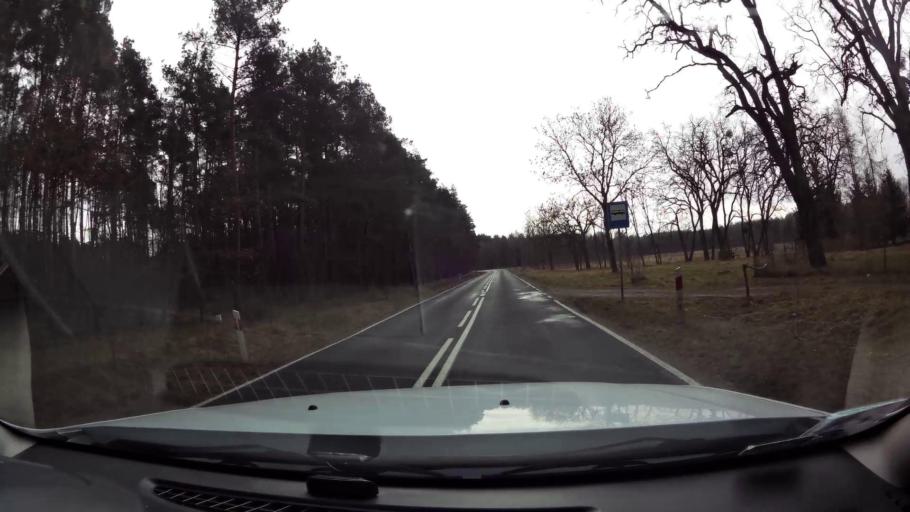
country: PL
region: West Pomeranian Voivodeship
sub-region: Powiat mysliborski
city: Debno
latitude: 52.7609
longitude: 14.6800
